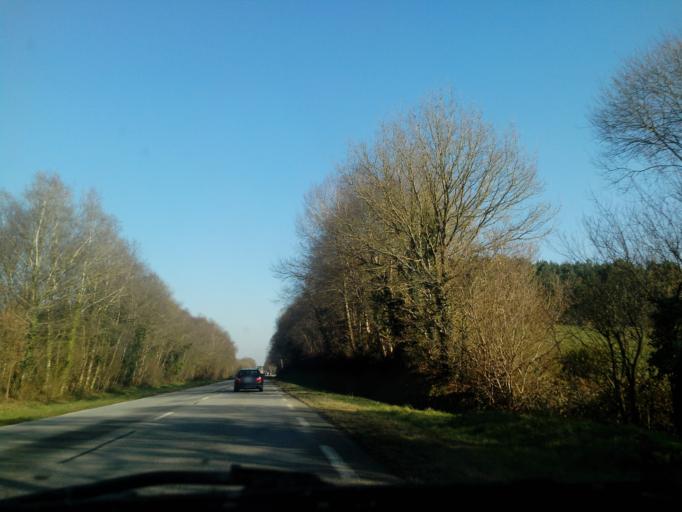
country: FR
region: Brittany
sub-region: Departement des Cotes-d'Armor
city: Plemet
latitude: 48.1833
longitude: -2.5432
